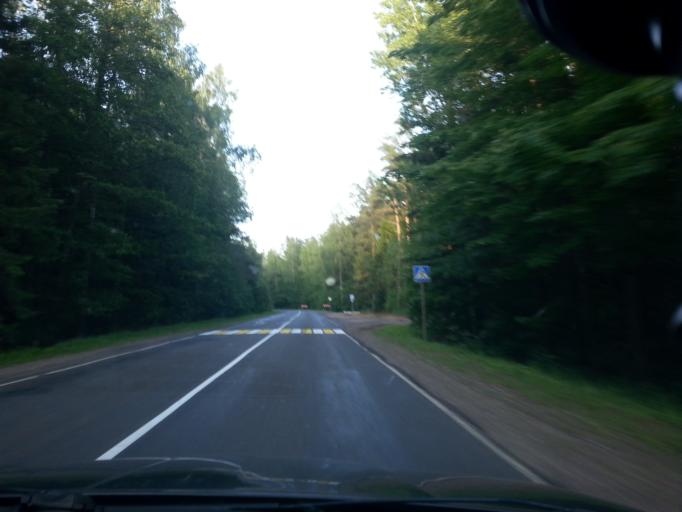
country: BY
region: Minsk
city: Svir
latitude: 54.9220
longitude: 26.5225
